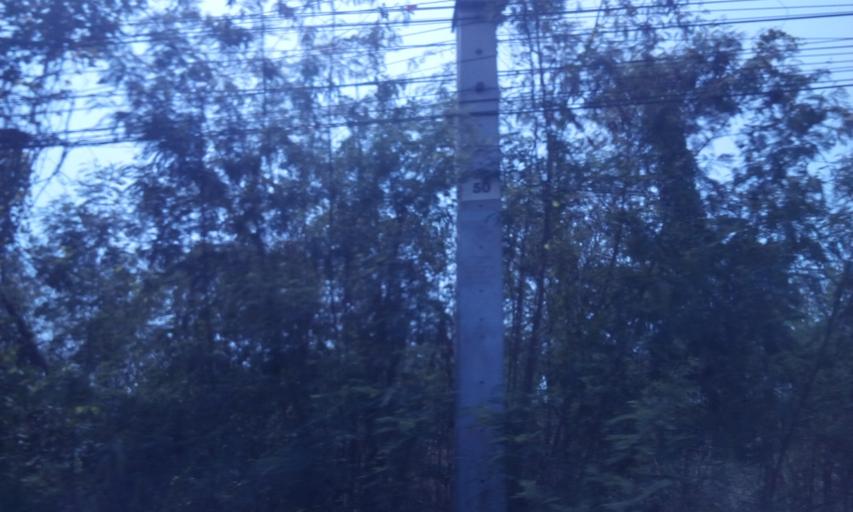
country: TH
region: Nonthaburi
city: Sai Noi
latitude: 13.9617
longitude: 100.3108
